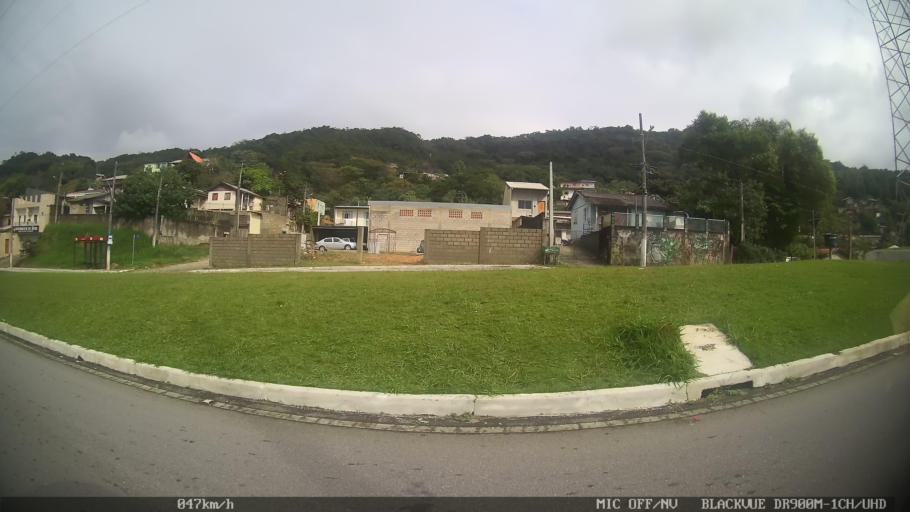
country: BR
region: Santa Catarina
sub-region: Biguacu
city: Biguacu
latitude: -27.5446
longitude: -48.6484
